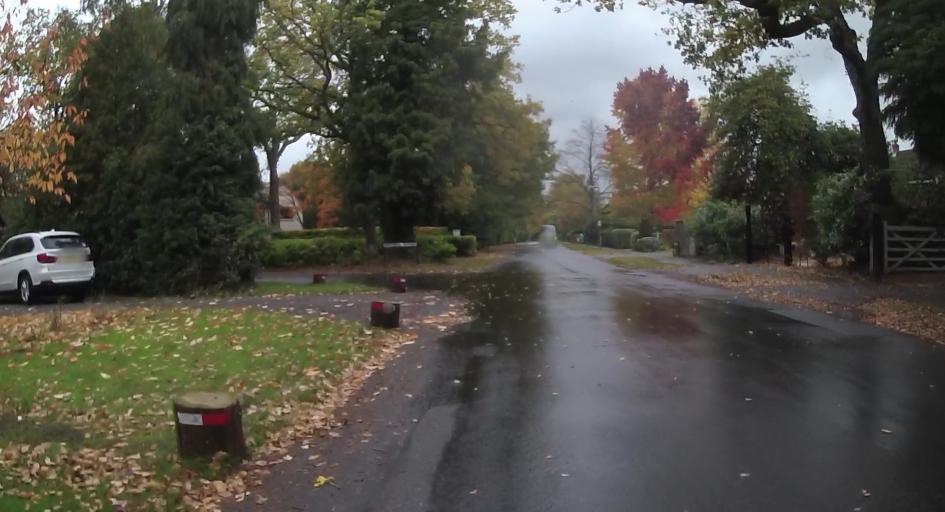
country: GB
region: England
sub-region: Surrey
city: Byfleet
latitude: 51.3429
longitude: -0.4882
